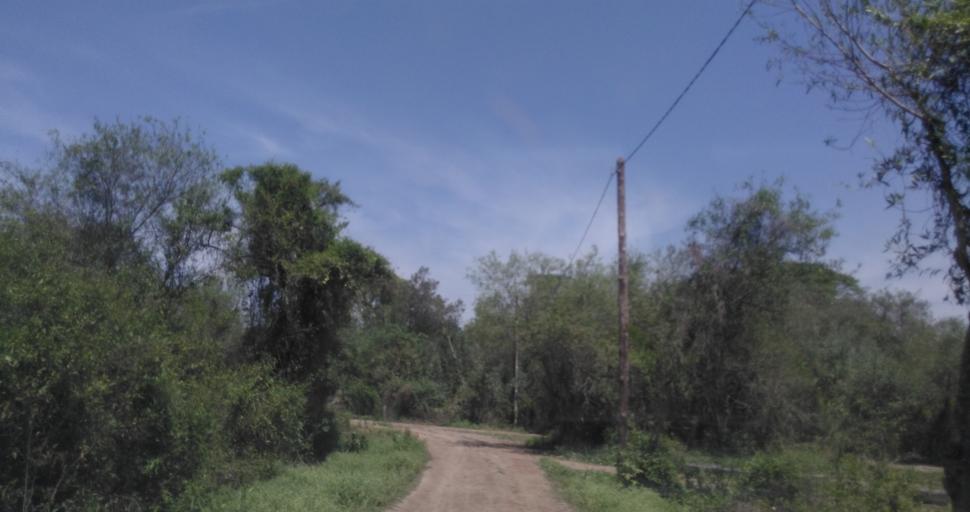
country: AR
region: Chaco
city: Fontana
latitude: -27.4101
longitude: -59.0138
